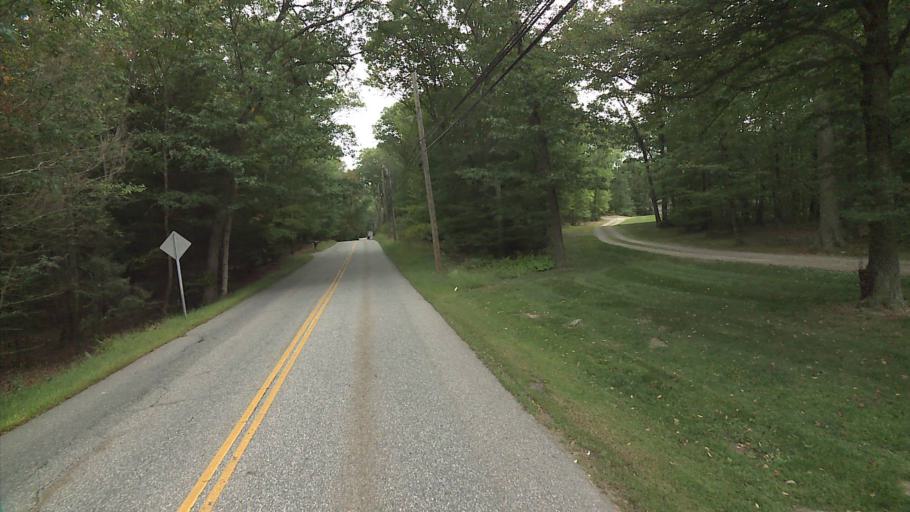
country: US
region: Connecticut
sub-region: Tolland County
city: Storrs
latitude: 41.7930
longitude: -72.2626
